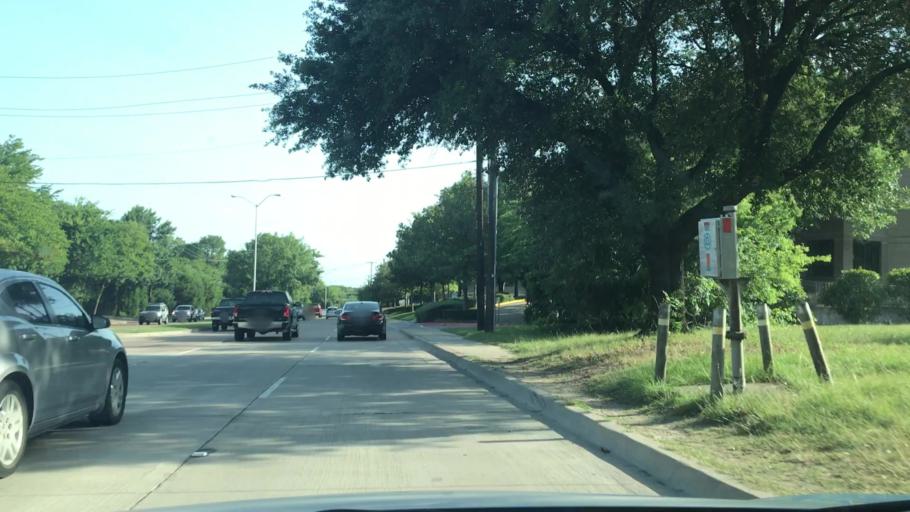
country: US
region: Texas
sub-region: Dallas County
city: Richardson
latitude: 32.9063
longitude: -96.7481
